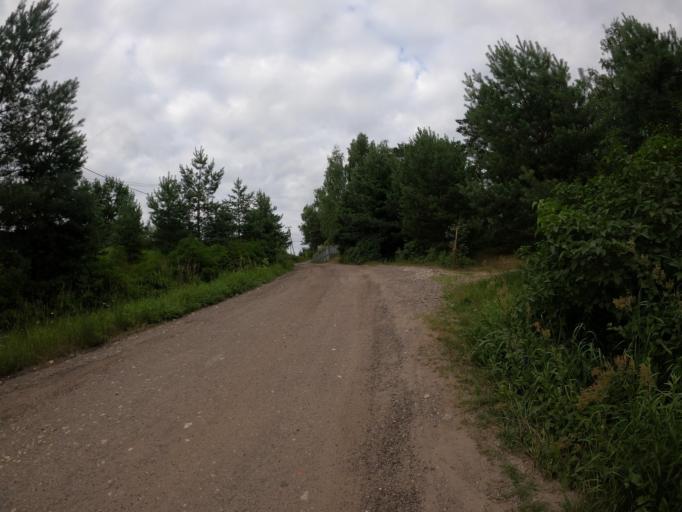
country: RU
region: Moskovskaya
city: Sychevo
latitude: 54.9076
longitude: 38.7303
